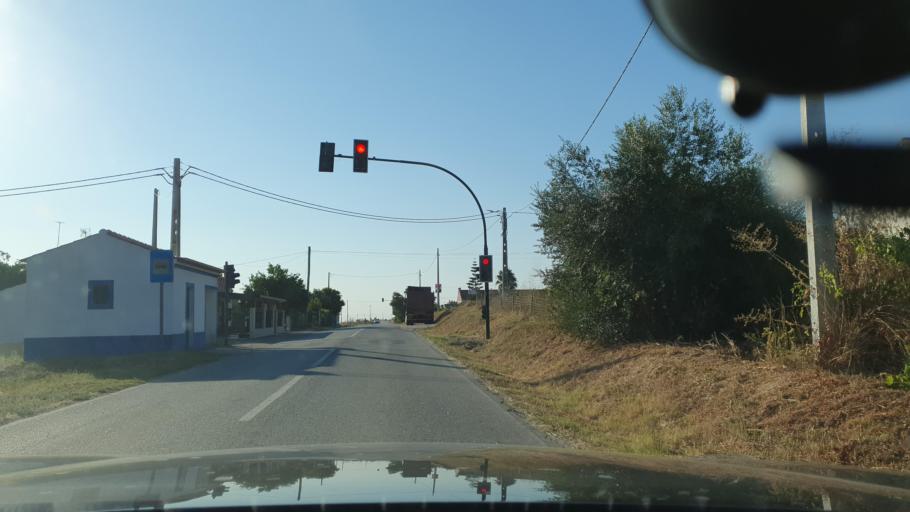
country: PT
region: Evora
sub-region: Estremoz
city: Estremoz
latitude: 38.8777
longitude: -7.6379
